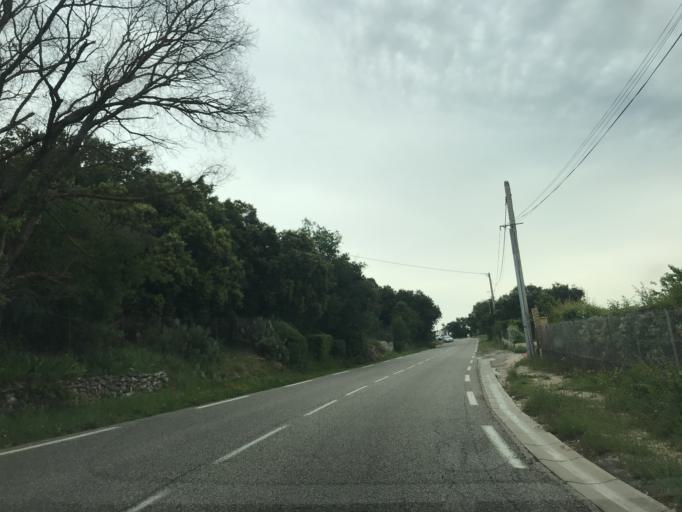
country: FR
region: Provence-Alpes-Cote d'Azur
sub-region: Departement du Var
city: Ginasservis
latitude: 43.6643
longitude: 5.8502
